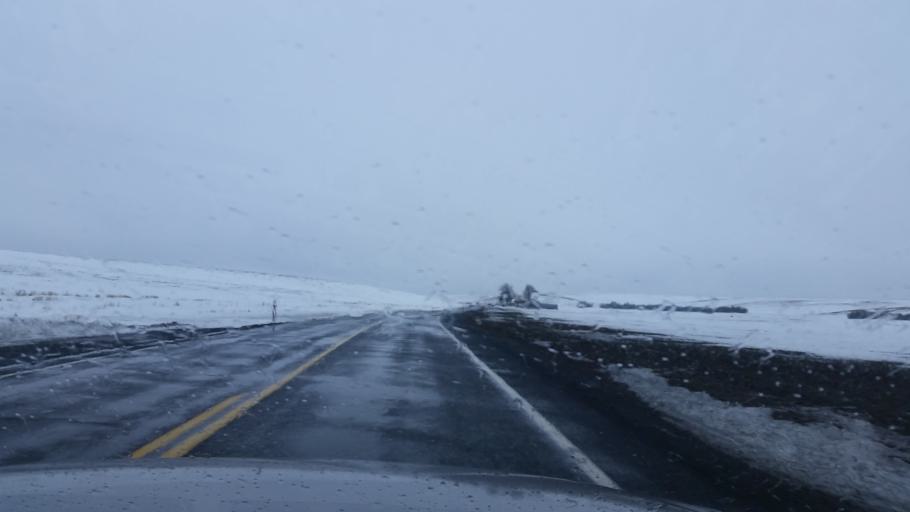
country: US
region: Washington
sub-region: Lincoln County
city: Davenport
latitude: 47.4264
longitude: -118.1850
